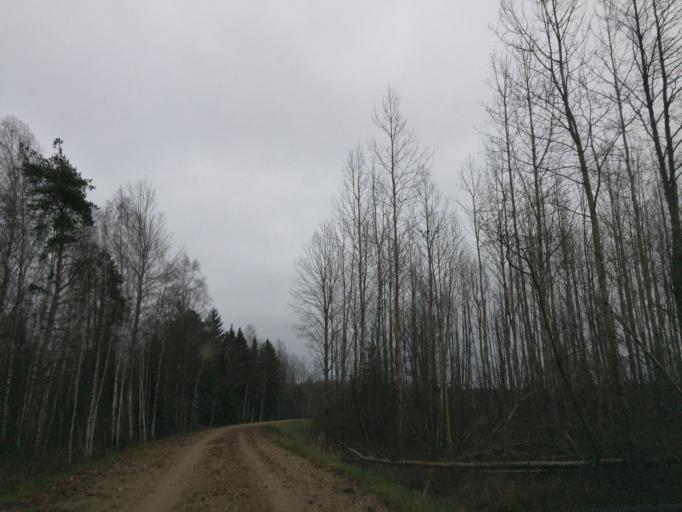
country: LV
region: Burtnieki
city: Matisi
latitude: 57.5464
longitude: 25.1536
